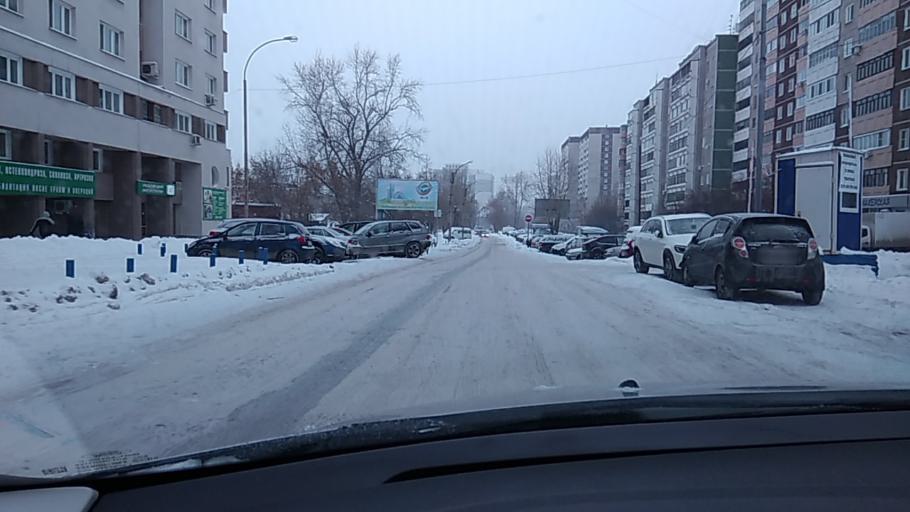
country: RU
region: Sverdlovsk
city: Yekaterinburg
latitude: 56.8079
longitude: 60.5985
